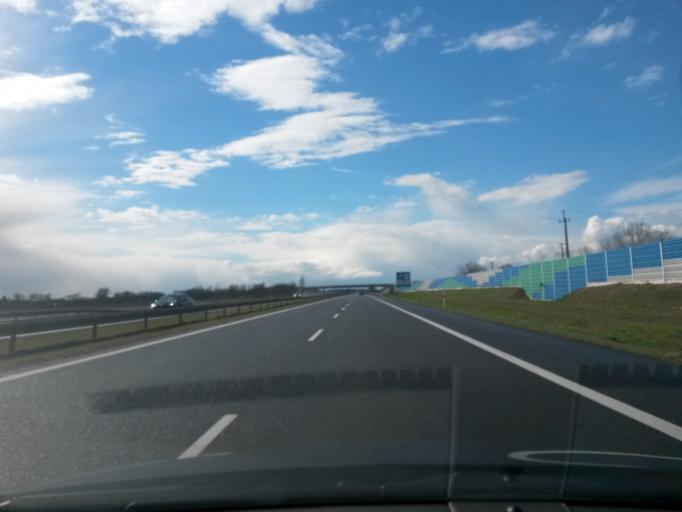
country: PL
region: Greater Poland Voivodeship
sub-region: Powiat slupecki
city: Strzalkowo
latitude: 52.2578
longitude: 17.8007
